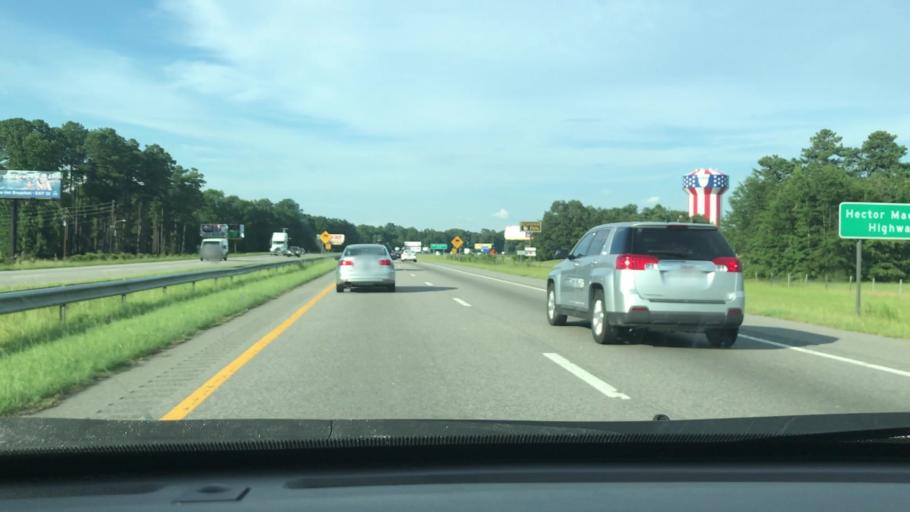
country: US
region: North Carolina
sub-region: Robeson County
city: Lumberton
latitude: 34.6184
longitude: -79.0641
